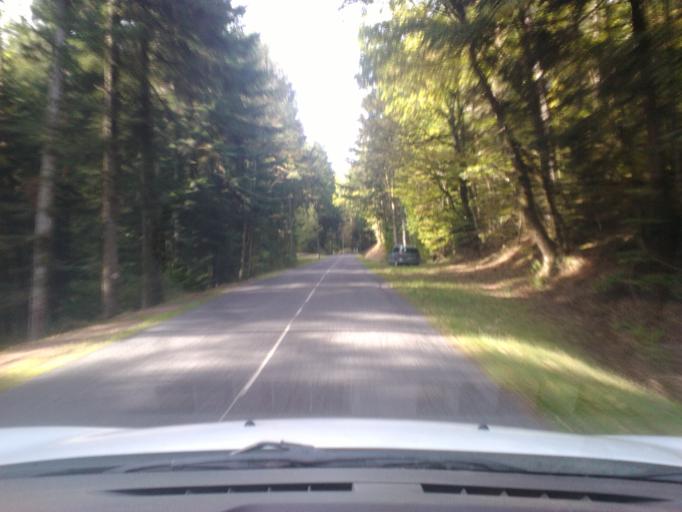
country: FR
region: Lorraine
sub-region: Departement des Vosges
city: Sainte-Marguerite
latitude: 48.2959
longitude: 6.9900
